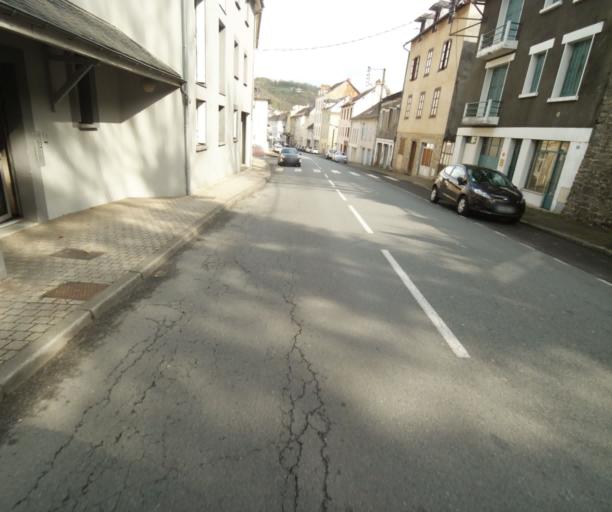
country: FR
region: Limousin
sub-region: Departement de la Correze
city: Tulle
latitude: 45.2597
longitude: 1.7502
